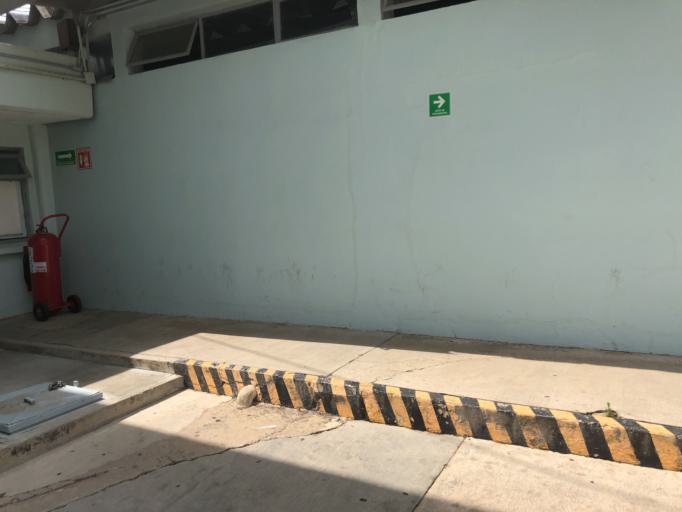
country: MX
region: Oaxaca
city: Oaxaca de Juarez
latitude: 17.0814
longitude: -96.7128
